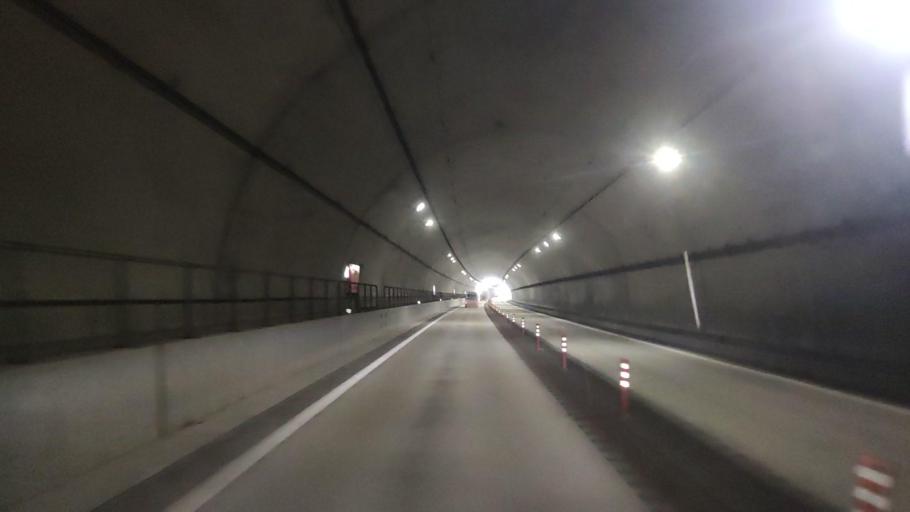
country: JP
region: Wakayama
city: Tanabe
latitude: 33.5951
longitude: 135.4355
